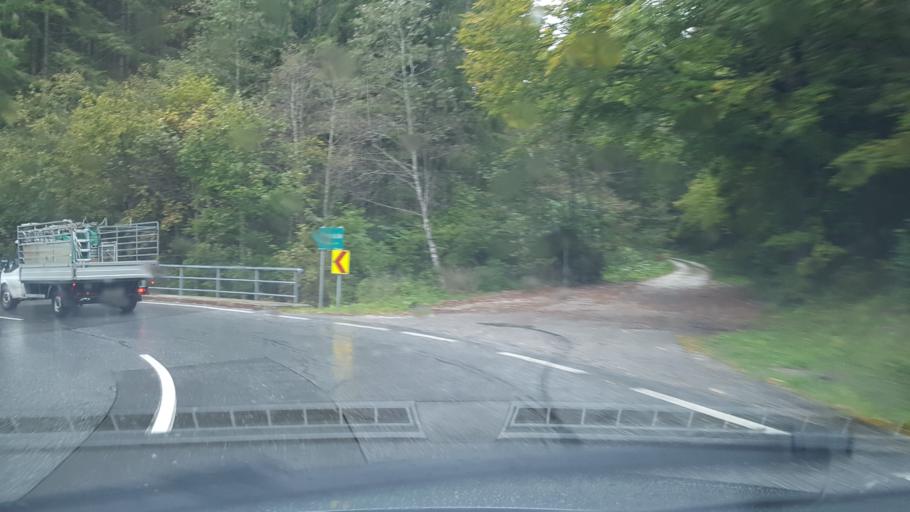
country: AT
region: Styria
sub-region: Politischer Bezirk Voitsberg
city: Salla
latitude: 47.1048
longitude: 14.9492
